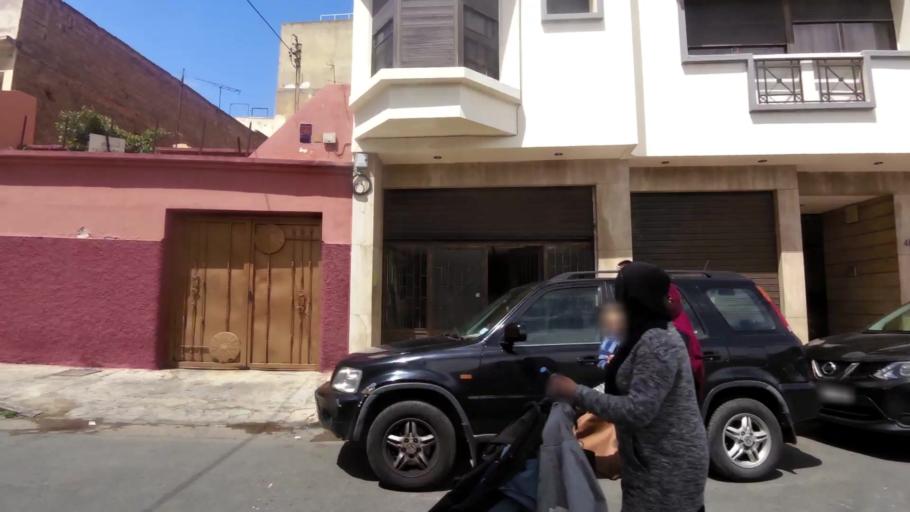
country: MA
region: Grand Casablanca
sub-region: Casablanca
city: Casablanca
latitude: 33.5973
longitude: -7.6380
